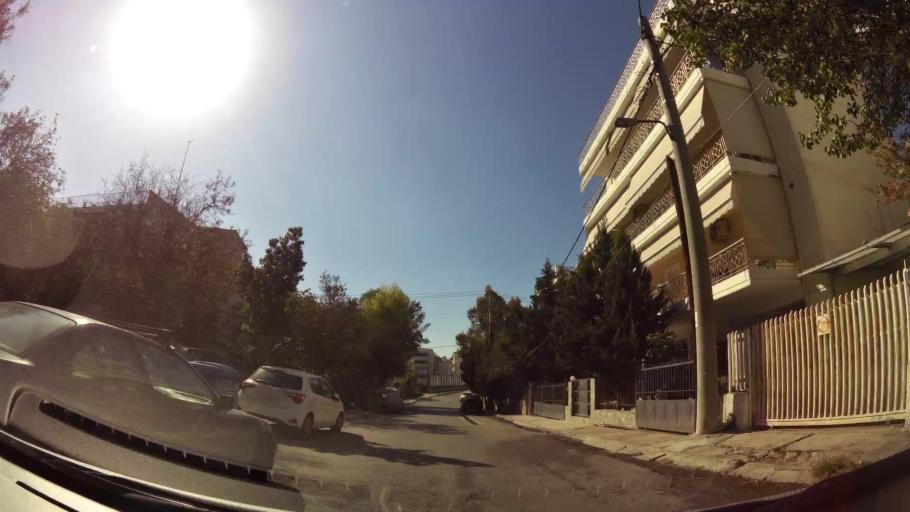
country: GR
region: Attica
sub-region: Nomarchia Athinas
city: Irakleio
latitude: 38.0594
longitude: 23.7689
